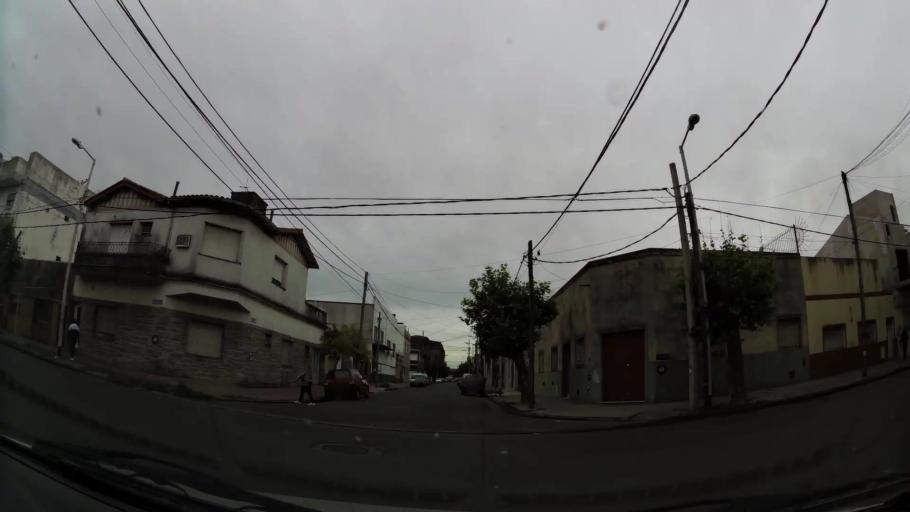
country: AR
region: Buenos Aires
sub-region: Partido de Avellaneda
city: Avellaneda
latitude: -34.6656
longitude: -58.3547
